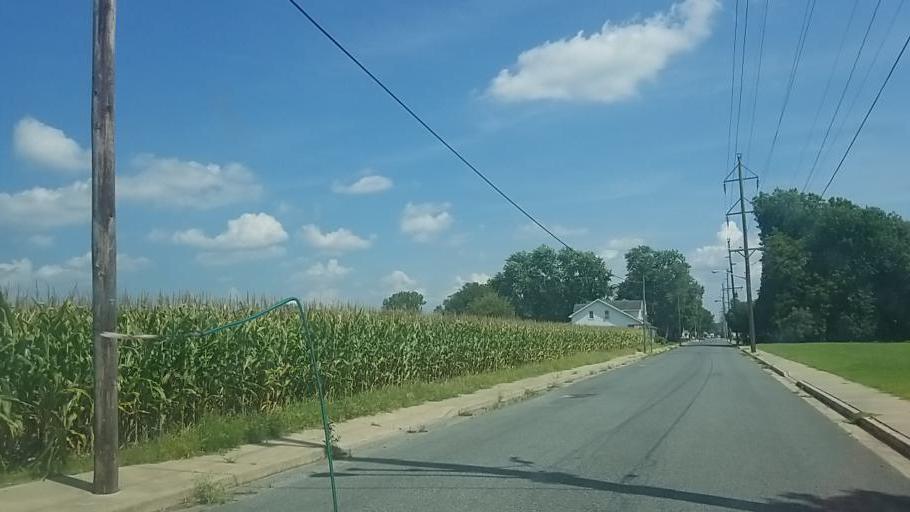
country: US
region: Maryland
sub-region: Wicomico County
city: Hebron
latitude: 38.4213
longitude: -75.6917
